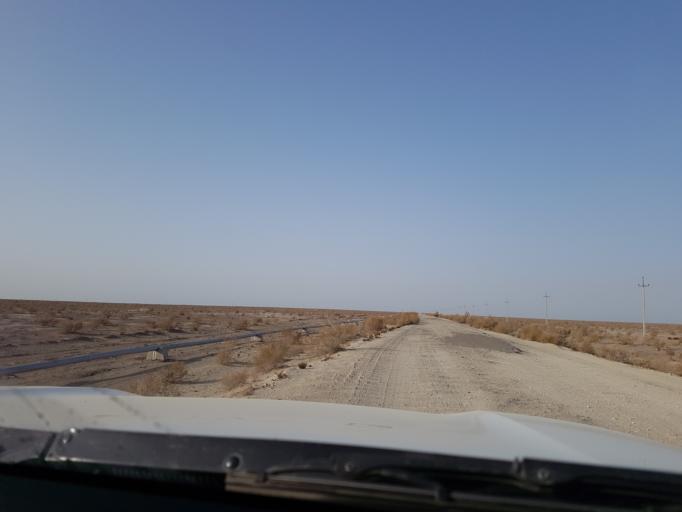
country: UZ
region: Karakalpakstan
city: Shumanay Shahri
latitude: 42.0084
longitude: 58.0876
